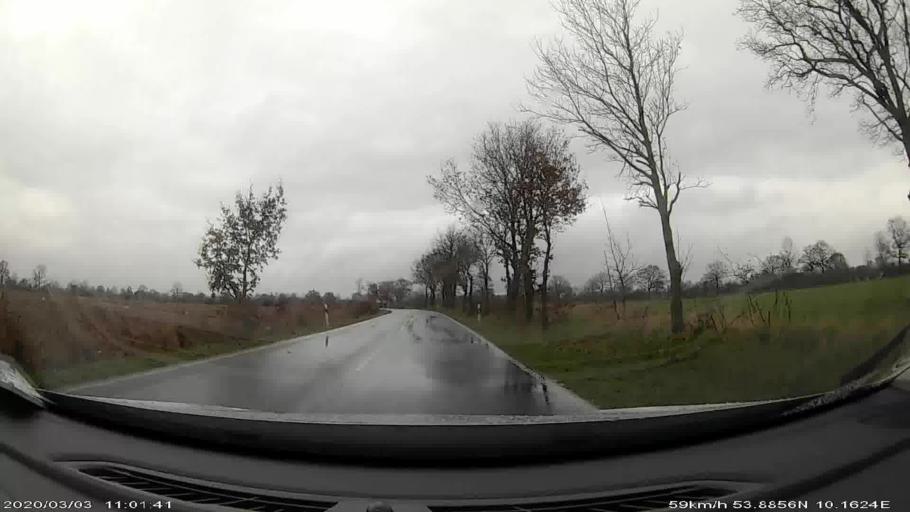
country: DE
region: Schleswig-Holstein
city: Todesfelde
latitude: 53.8885
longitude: 10.1642
